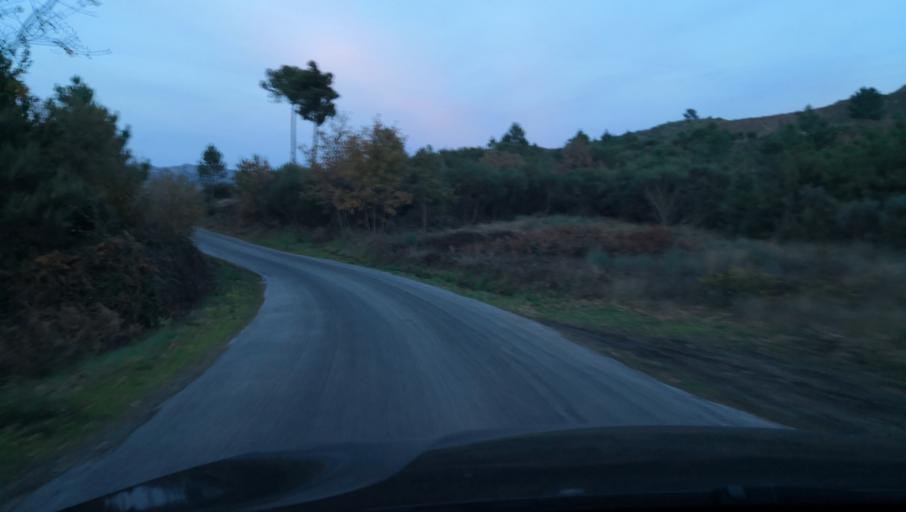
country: PT
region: Vila Real
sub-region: Vila Real
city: Vila Real
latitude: 41.3460
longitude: -7.7017
